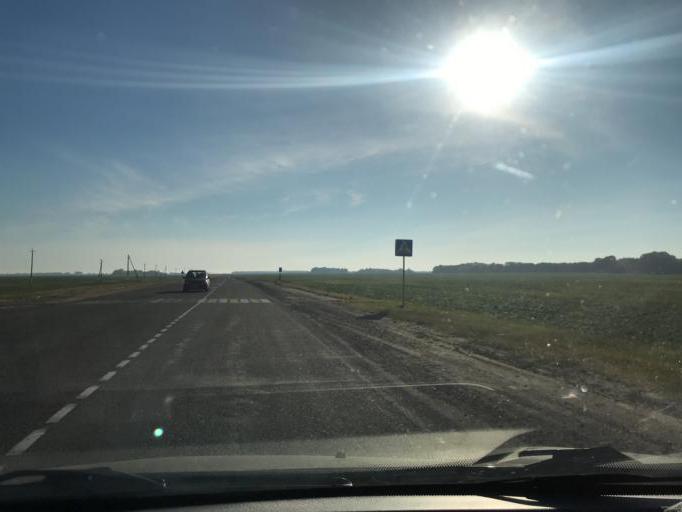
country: BY
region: Gomel
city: Brahin
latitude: 51.7971
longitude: 30.1449
